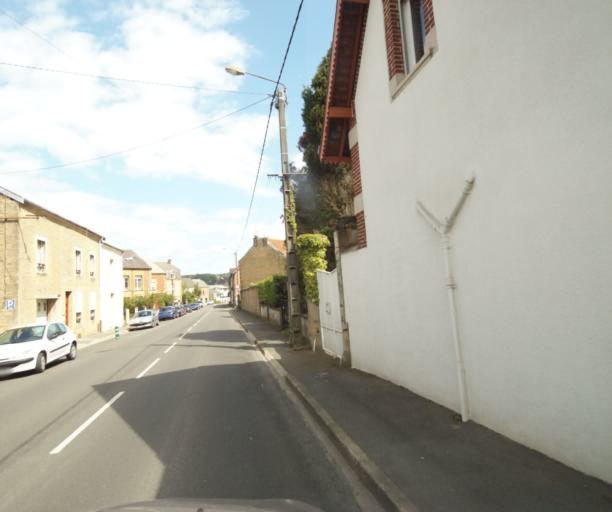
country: FR
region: Champagne-Ardenne
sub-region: Departement des Ardennes
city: Montcy-Notre-Dame
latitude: 49.7750
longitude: 4.7339
